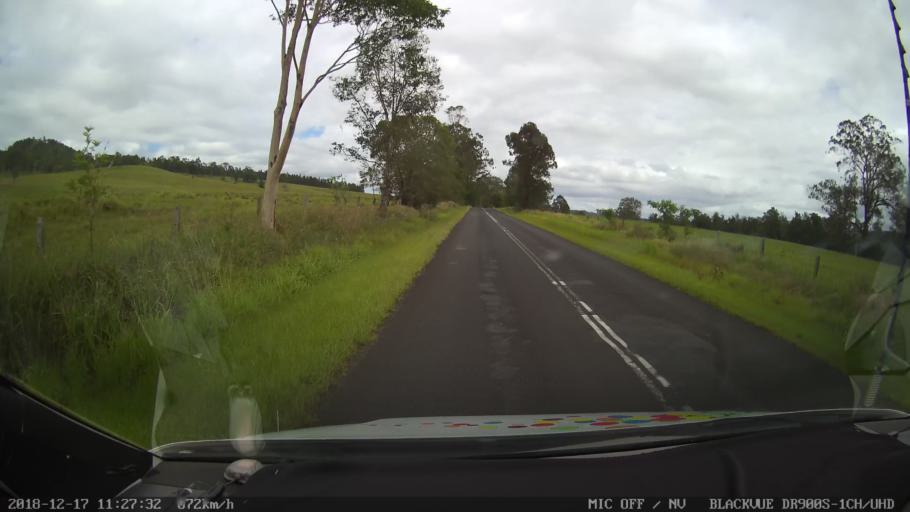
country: AU
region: New South Wales
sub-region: Kyogle
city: Kyogle
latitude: -28.7476
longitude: 152.6459
